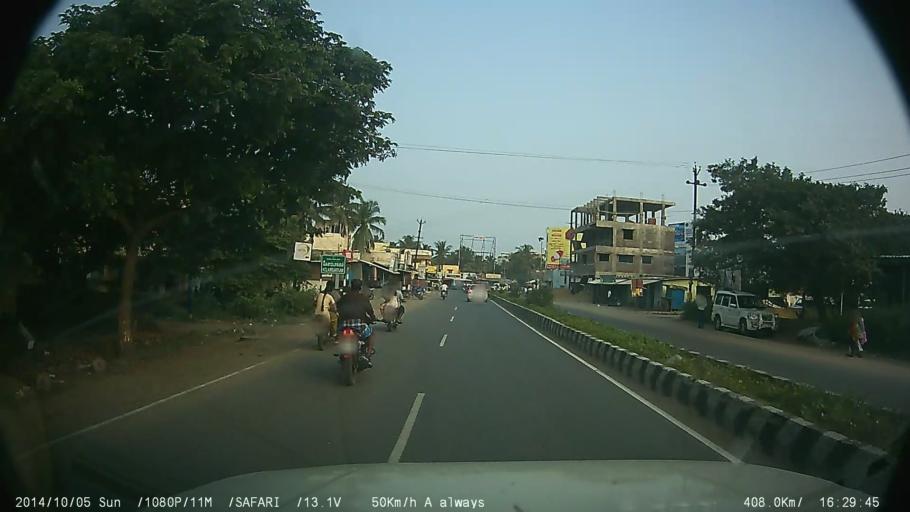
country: IN
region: Tamil Nadu
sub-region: Kancheepuram
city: Vengavasal
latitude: 12.7904
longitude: 80.2206
